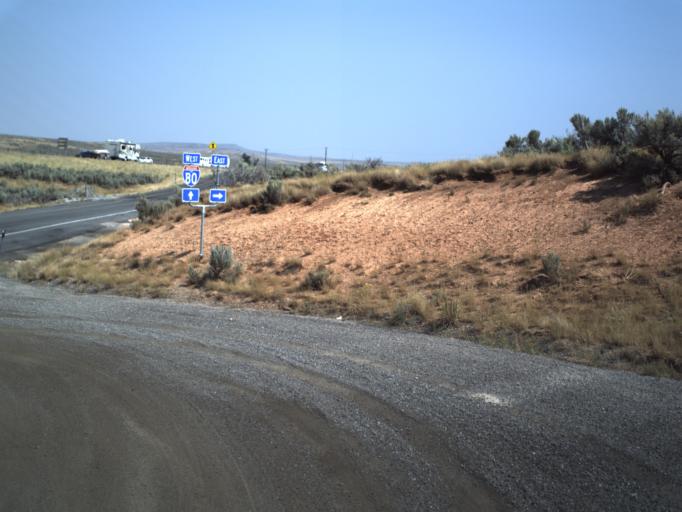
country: US
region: Wyoming
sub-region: Uinta County
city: Evanston
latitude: 41.2001
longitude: -111.1076
